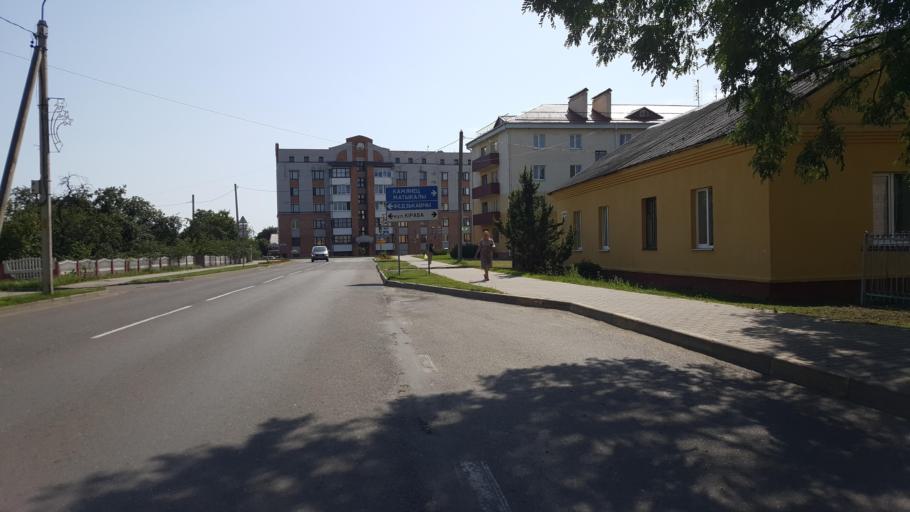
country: BY
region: Brest
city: Zhabinka
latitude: 52.1962
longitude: 24.0160
